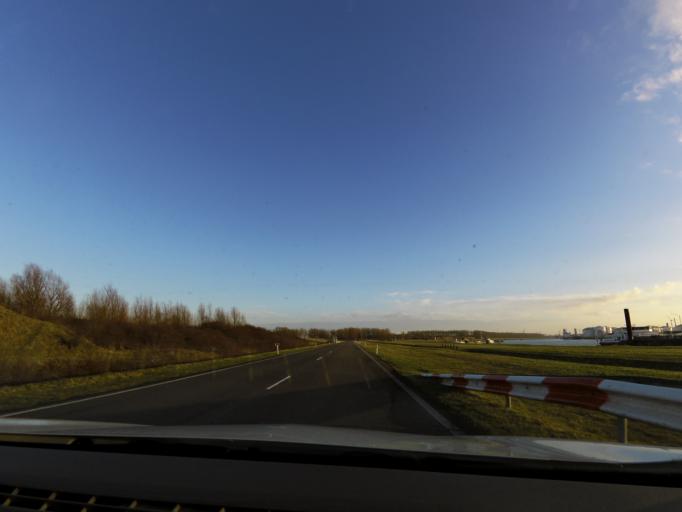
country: NL
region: South Holland
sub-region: Gemeente Westland
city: Maasdijk
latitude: 51.9253
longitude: 4.2145
